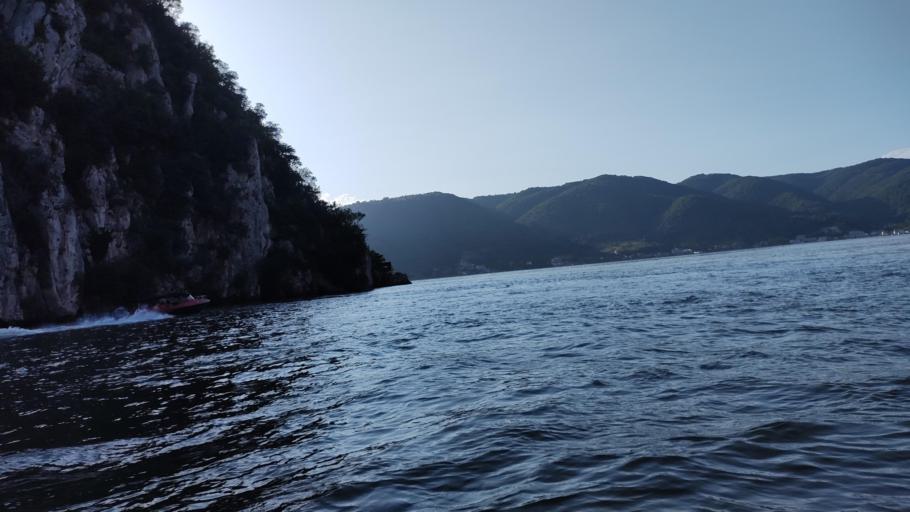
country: RO
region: Mehedinti
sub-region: Comuna Dubova
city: Dubova
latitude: 44.6159
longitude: 22.2727
